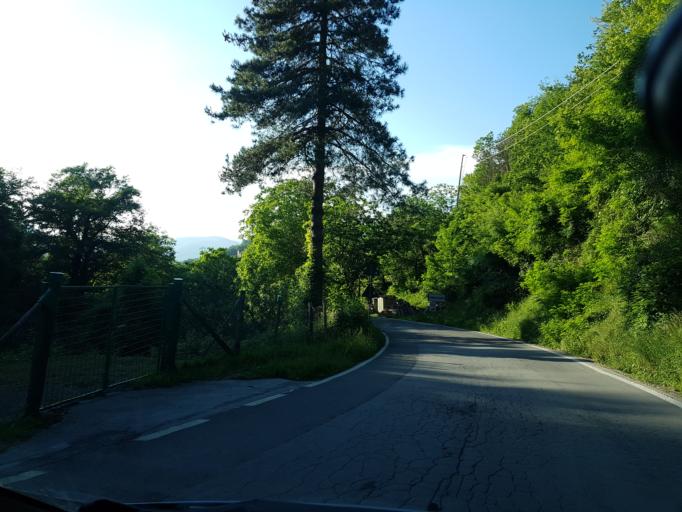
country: IT
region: Tuscany
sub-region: Provincia di Lucca
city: Minucciano
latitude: 44.1674
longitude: 10.2100
